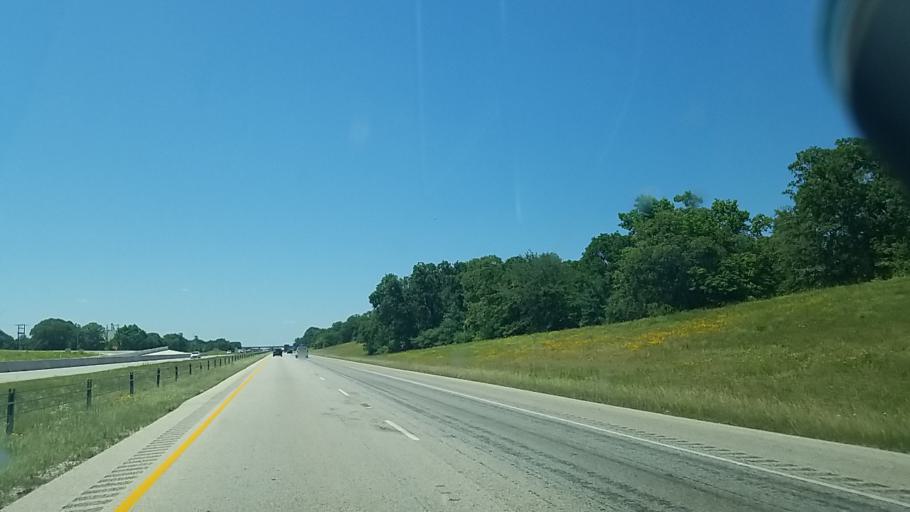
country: US
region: Texas
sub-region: Leon County
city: Buffalo
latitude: 31.4368
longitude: -96.0631
